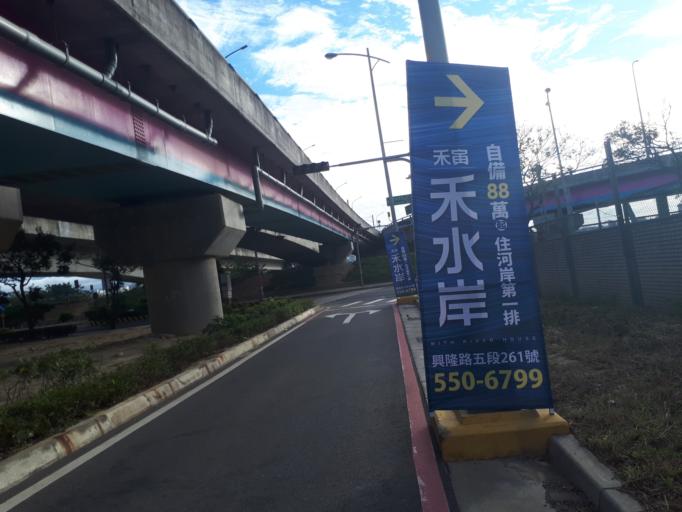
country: TW
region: Taiwan
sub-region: Hsinchu
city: Zhubei
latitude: 24.8000
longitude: 121.0376
